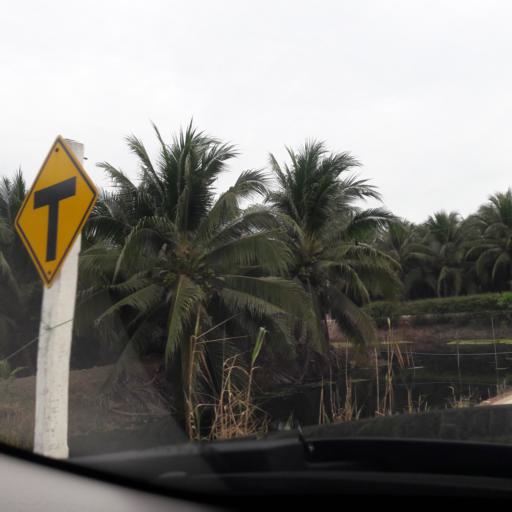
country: TH
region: Ratchaburi
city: Damnoen Saduak
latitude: 13.5797
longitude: 99.9392
